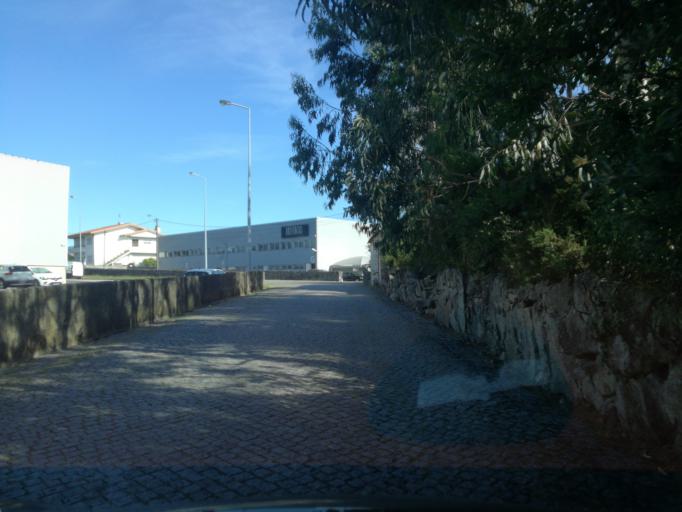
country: PT
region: Porto
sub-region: Maia
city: Anta
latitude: 41.2775
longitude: -8.6043
